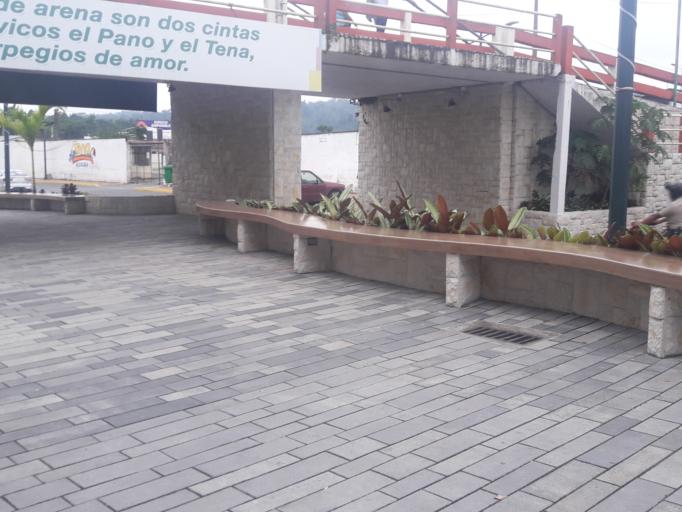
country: EC
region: Napo
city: Tena
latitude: -0.9920
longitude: -77.8149
